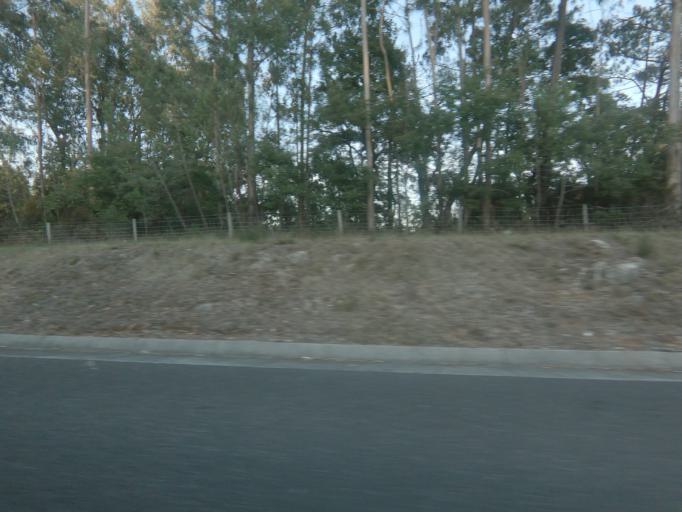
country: PT
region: Leiria
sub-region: Leiria
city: Santa Catarina da Serra
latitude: 39.6532
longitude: -8.6961
